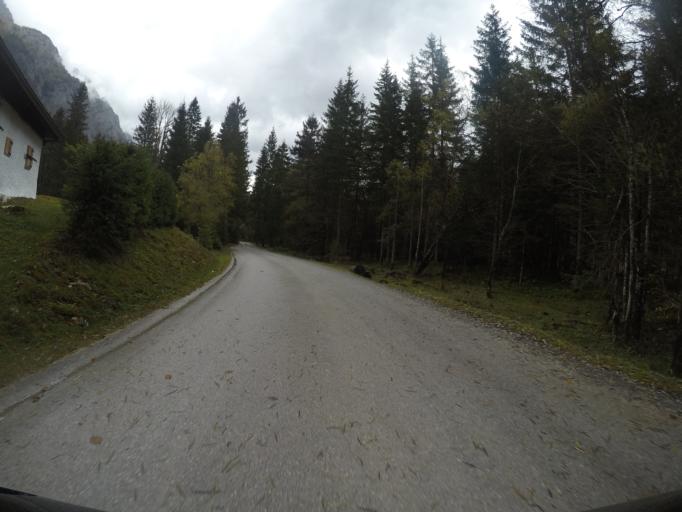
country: SI
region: Kranjska Gora
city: Mojstrana
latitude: 46.4169
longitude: 13.8556
